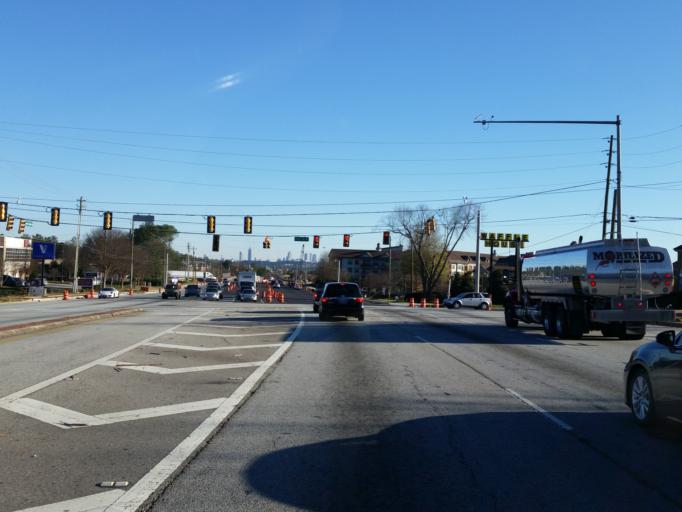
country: US
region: Georgia
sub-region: Cobb County
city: Vinings
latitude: 33.8458
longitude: -84.4912
